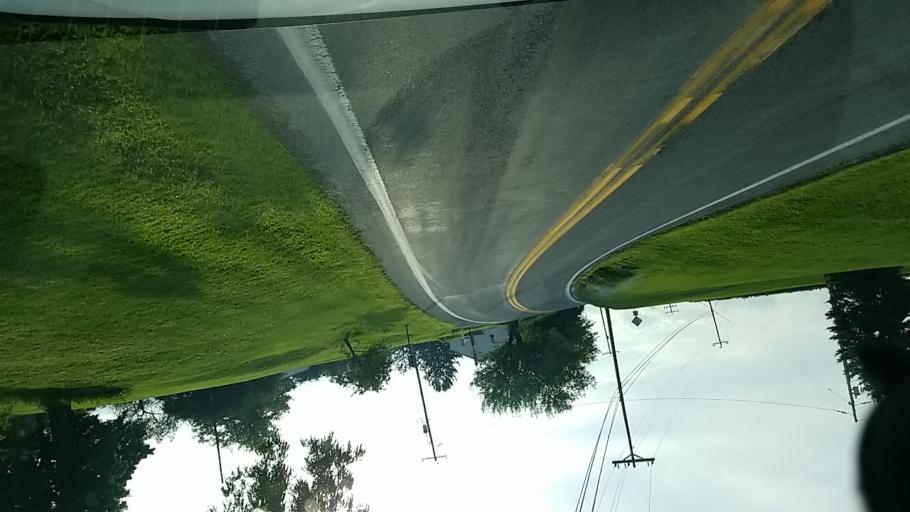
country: US
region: Pennsylvania
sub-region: Cumberland County
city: Newville
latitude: 40.2373
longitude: -77.4472
